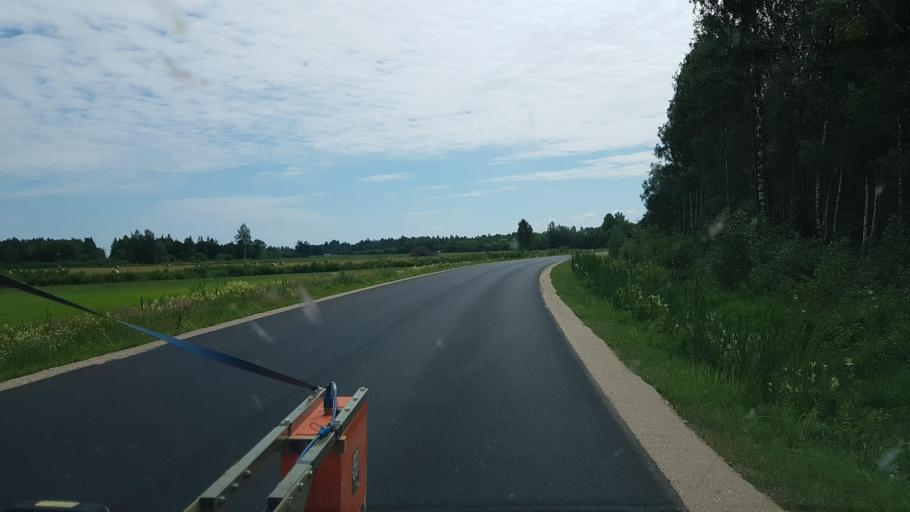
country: EE
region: Paernumaa
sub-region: Audru vald
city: Audru
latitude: 58.6216
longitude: 24.2703
